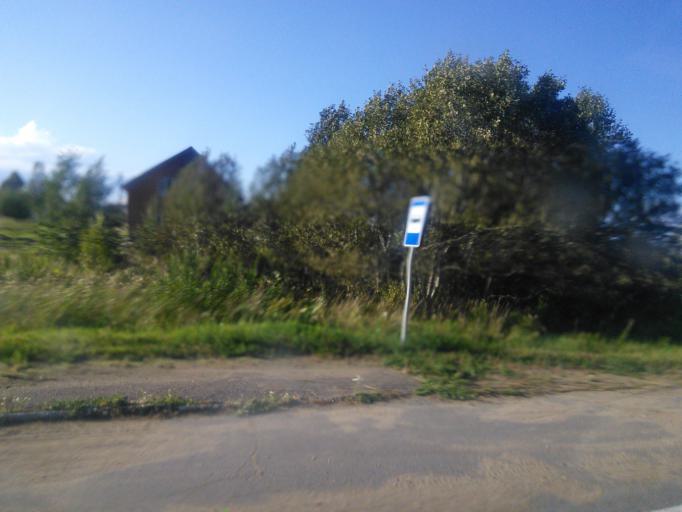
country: RU
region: Jaroslavl
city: Poshekhon'ye
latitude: 58.4234
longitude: 38.9914
